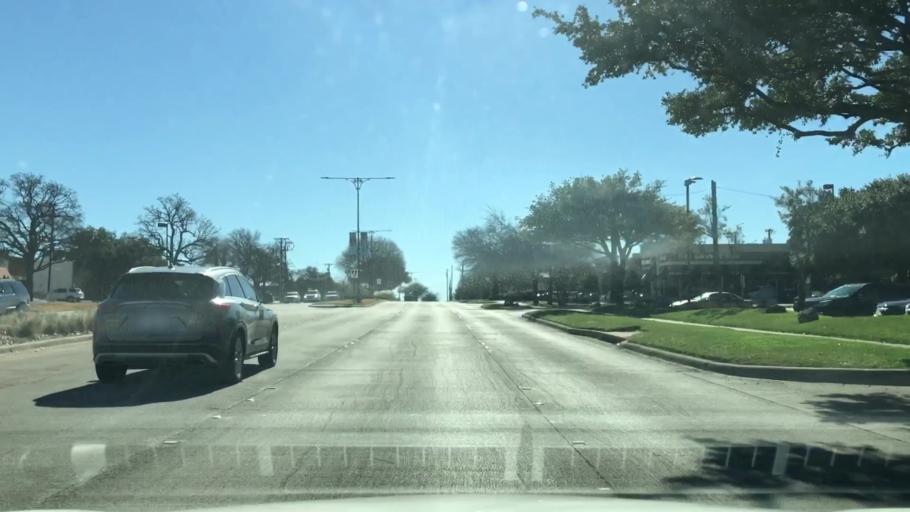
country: US
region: Texas
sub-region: Dallas County
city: Coppell
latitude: 32.9685
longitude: -96.9937
